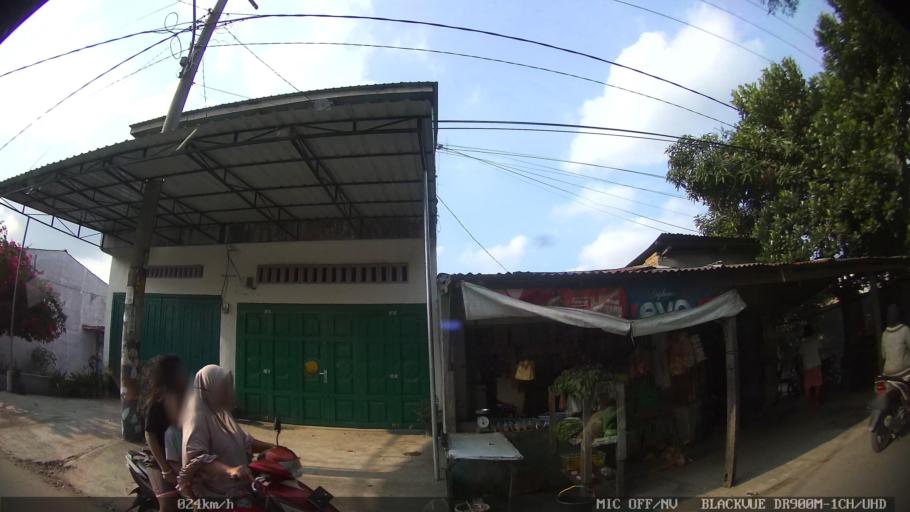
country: ID
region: North Sumatra
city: Medan
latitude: 3.5813
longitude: 98.7551
